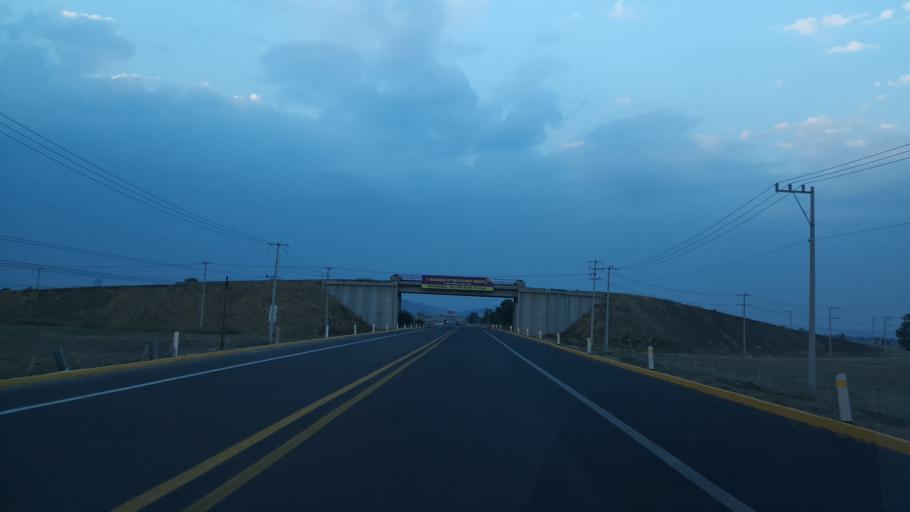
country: MX
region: Puebla
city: Santa Ana Xalmimilulco
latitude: 19.1861
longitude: -98.3698
